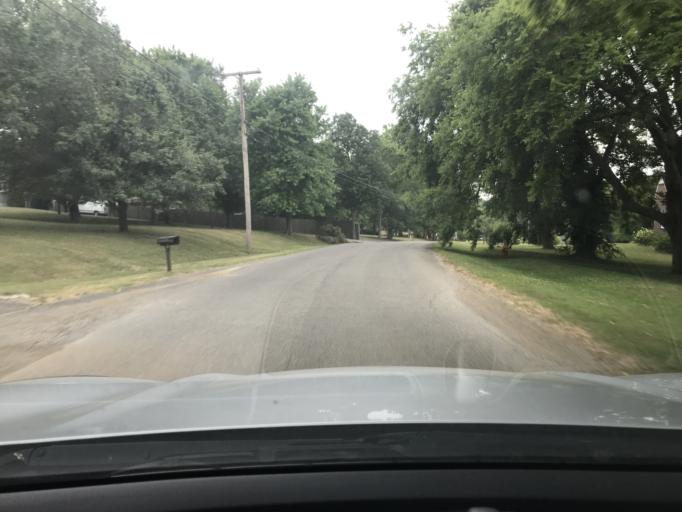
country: US
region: Tennessee
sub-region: Davidson County
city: Goodlettsville
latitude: 36.3038
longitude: -86.7171
